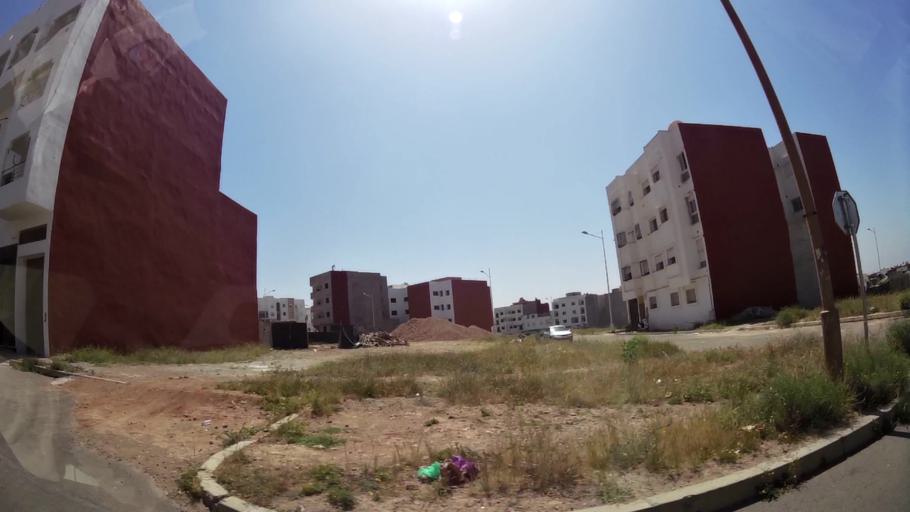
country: MA
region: Oued ed Dahab-Lagouira
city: Dakhla
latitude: 30.4328
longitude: -9.5598
